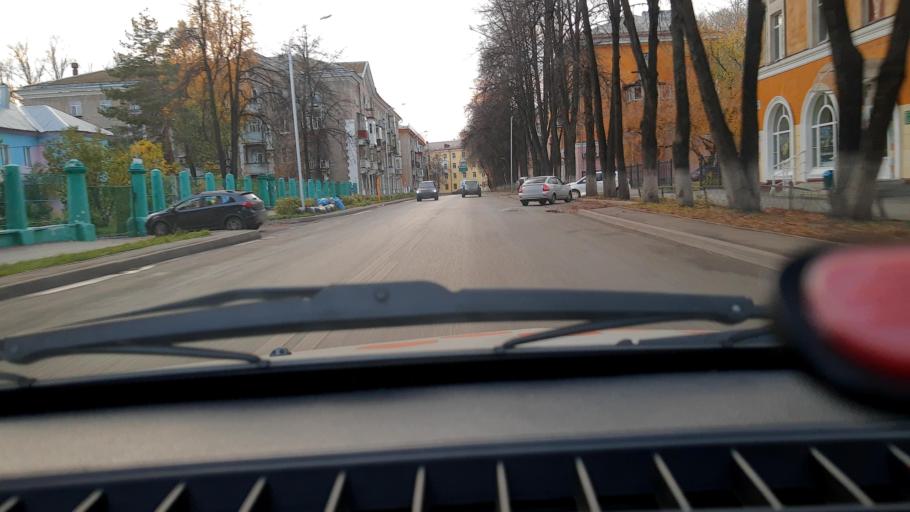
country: RU
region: Bashkortostan
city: Ufa
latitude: 54.8204
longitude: 56.0747
